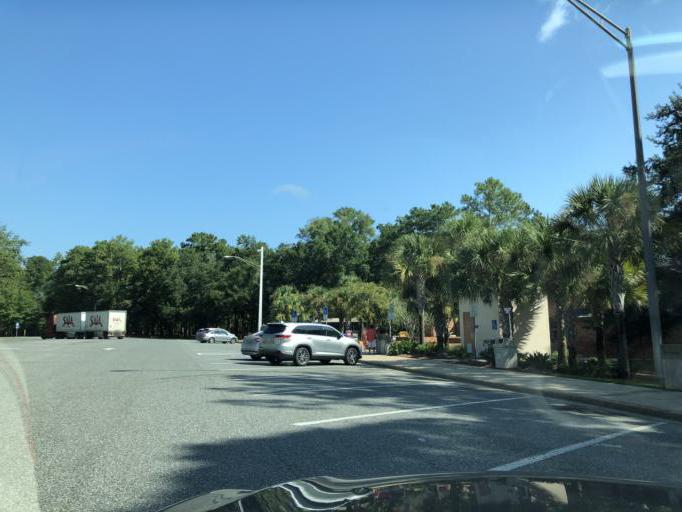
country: US
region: Florida
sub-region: Walton County
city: DeFuniak Springs
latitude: 30.7125
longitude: -85.9302
